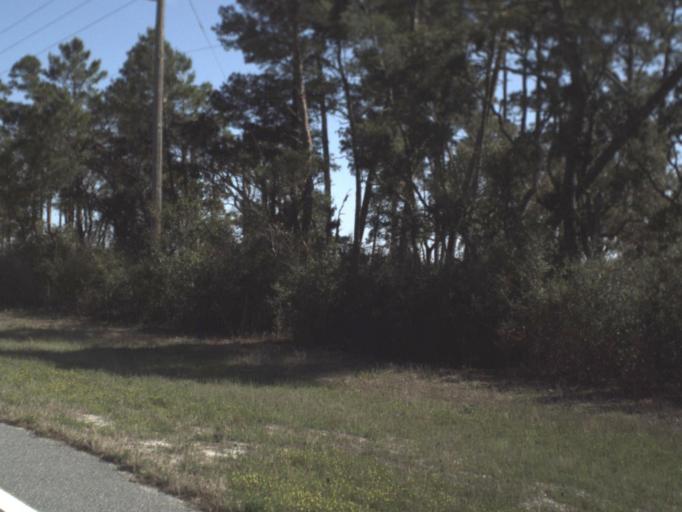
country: US
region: Florida
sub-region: Franklin County
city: Carrabelle
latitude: 29.9274
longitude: -84.4308
